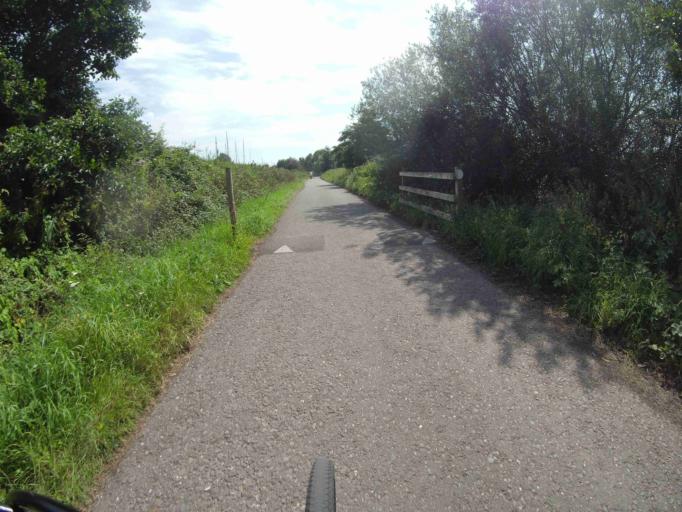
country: GB
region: England
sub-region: Devon
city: Topsham
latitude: 50.6661
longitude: -3.4685
